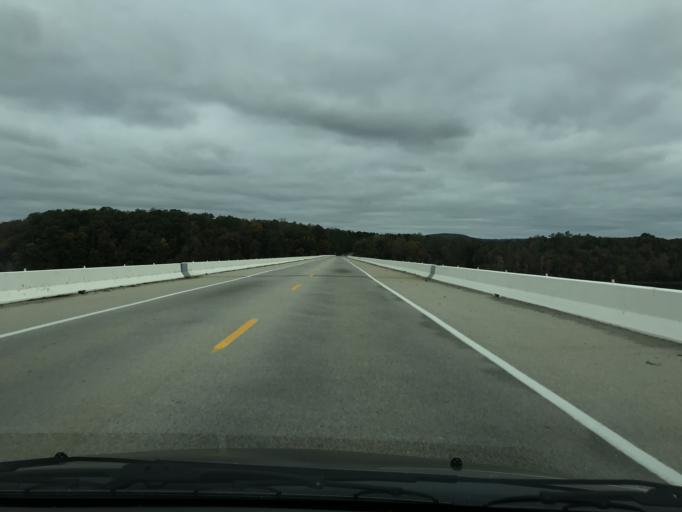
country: US
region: Tennessee
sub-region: Rhea County
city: Graysville
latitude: 35.4102
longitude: -85.0194
